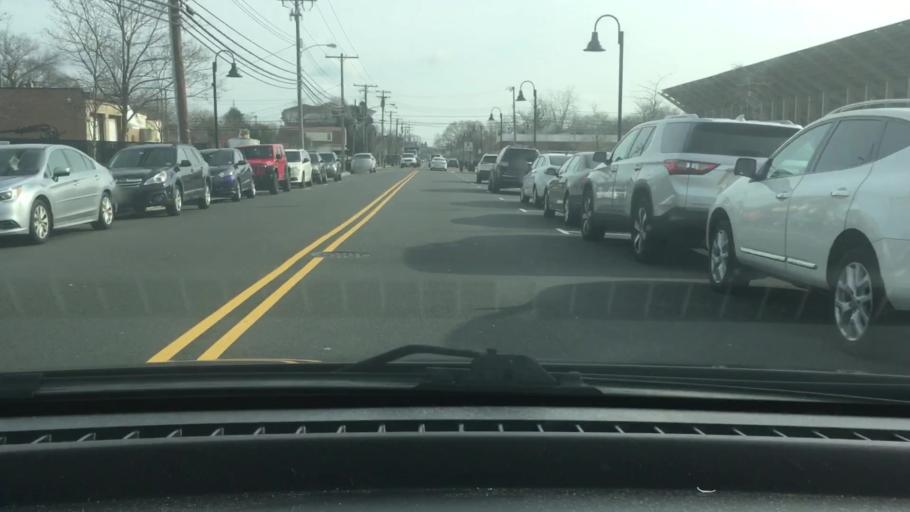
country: US
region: New Jersey
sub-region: Monmouth County
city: Neptune City
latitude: 40.2157
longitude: -74.0295
